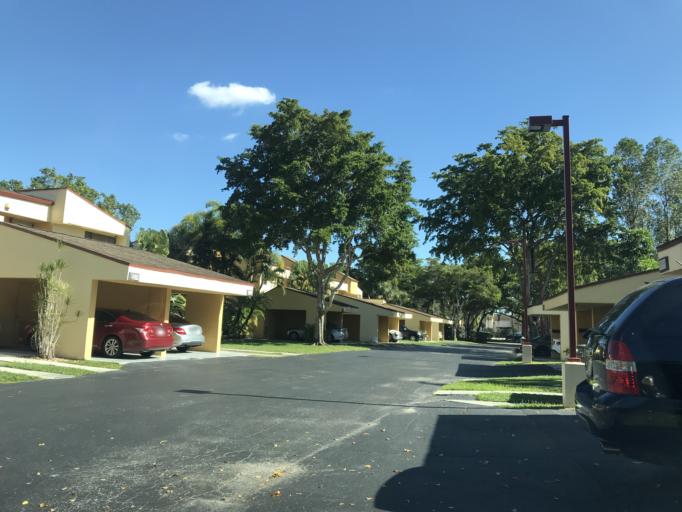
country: US
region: Florida
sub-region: Broward County
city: Plantation
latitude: 26.1350
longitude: -80.2642
